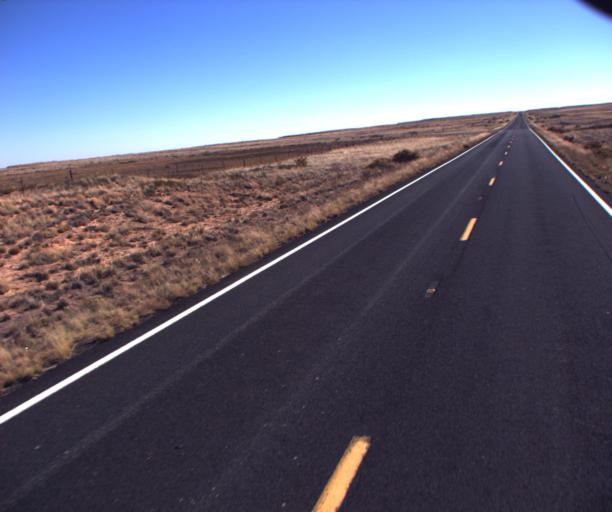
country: US
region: Arizona
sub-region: Coconino County
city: Tuba City
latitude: 35.9866
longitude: -111.0026
